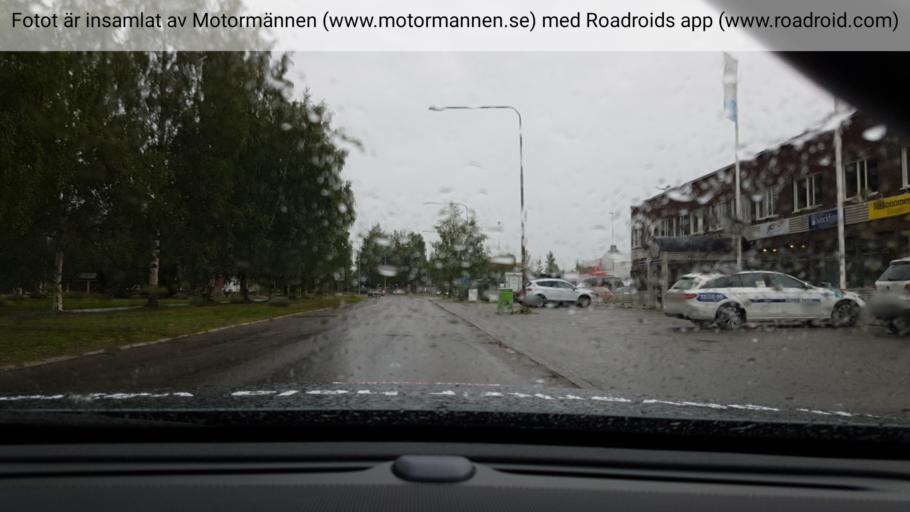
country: SE
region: Vaesterbotten
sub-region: Umea Kommun
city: Umea
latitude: 63.8174
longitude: 20.2467
